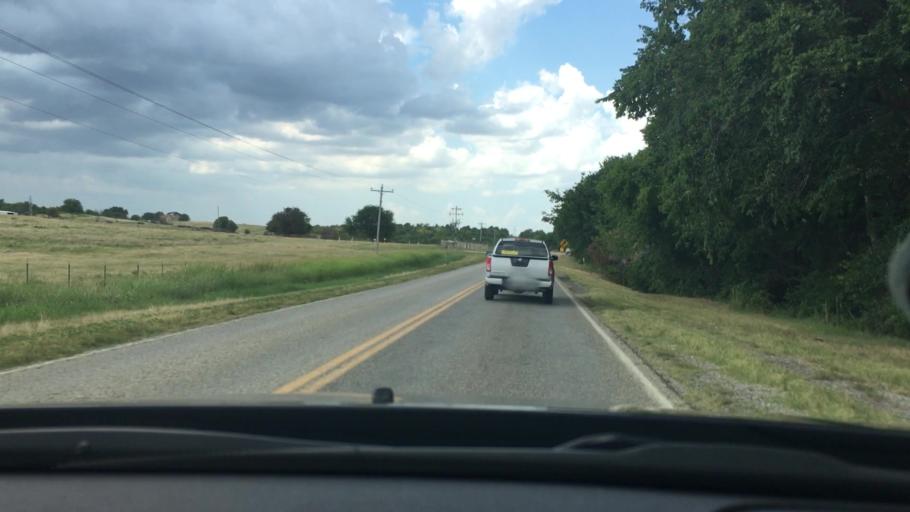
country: US
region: Oklahoma
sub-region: Pontotoc County
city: Ada
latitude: 34.5614
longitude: -96.6346
